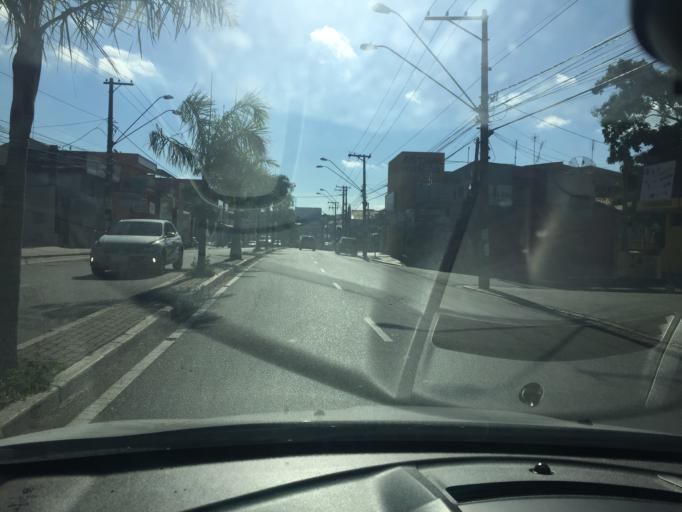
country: BR
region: Sao Paulo
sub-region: Varzea Paulista
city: Varzea Paulista
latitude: -23.2128
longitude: -46.8358
